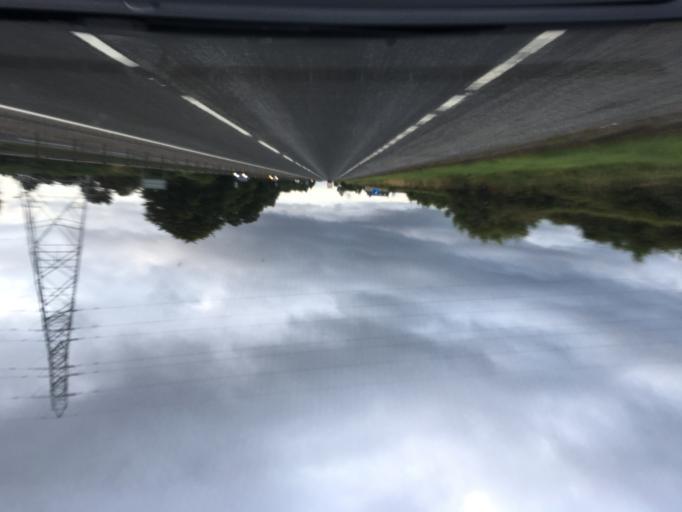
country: GB
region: Scotland
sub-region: Highland
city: Inverness
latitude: 57.4509
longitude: -4.1575
